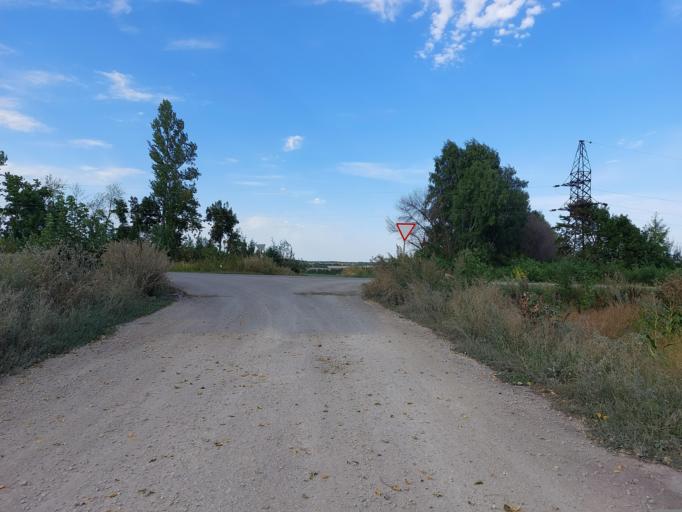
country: RU
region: Lipetsk
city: Dolgorukovo
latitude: 52.3153
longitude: 38.1595
